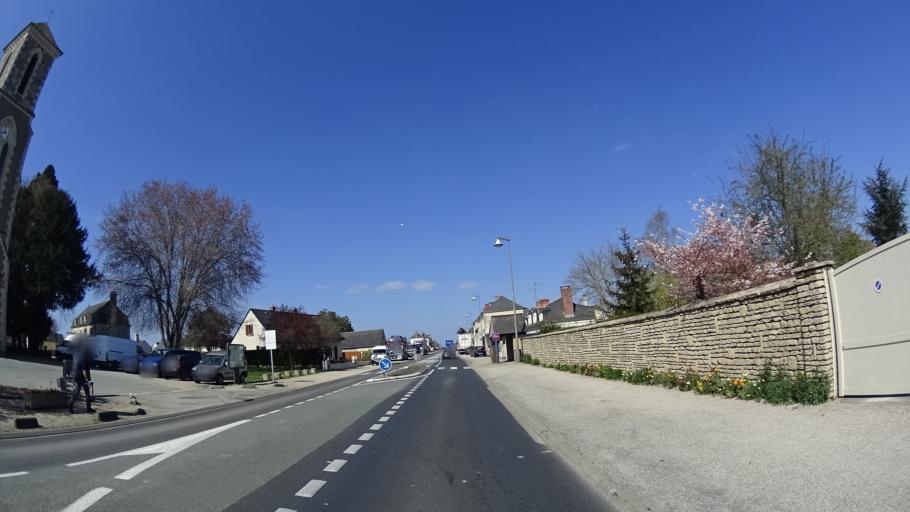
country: FR
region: Pays de la Loire
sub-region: Departement de Maine-et-Loire
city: Brissac-Quince
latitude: 47.3184
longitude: -0.4081
